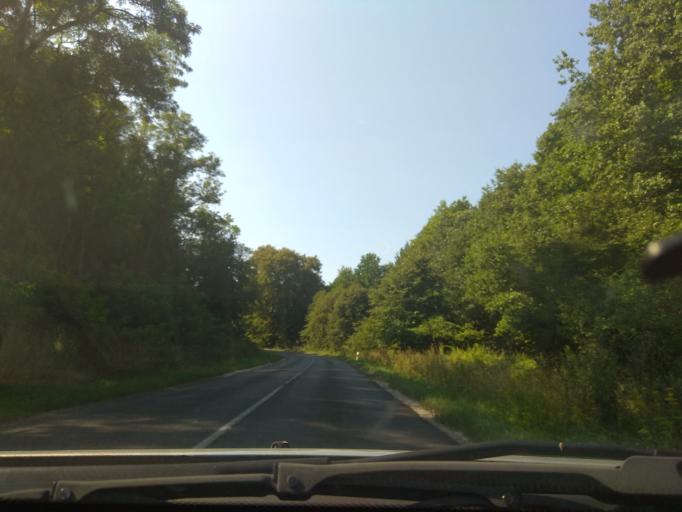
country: HU
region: Borsod-Abauj-Zemplen
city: Harsany
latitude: 47.9949
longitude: 20.7540
